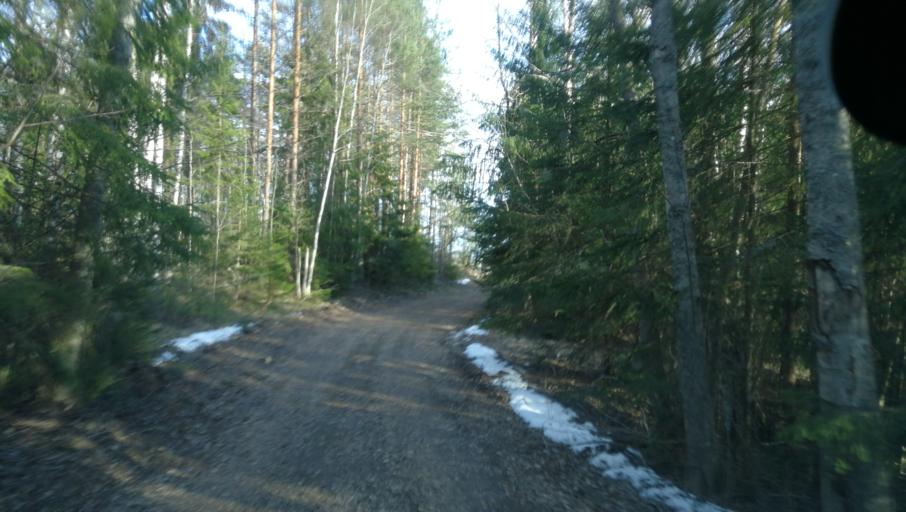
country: SE
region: Dalarna
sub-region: Vansbro Kommun
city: Vansbro
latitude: 60.7954
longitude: 14.2340
